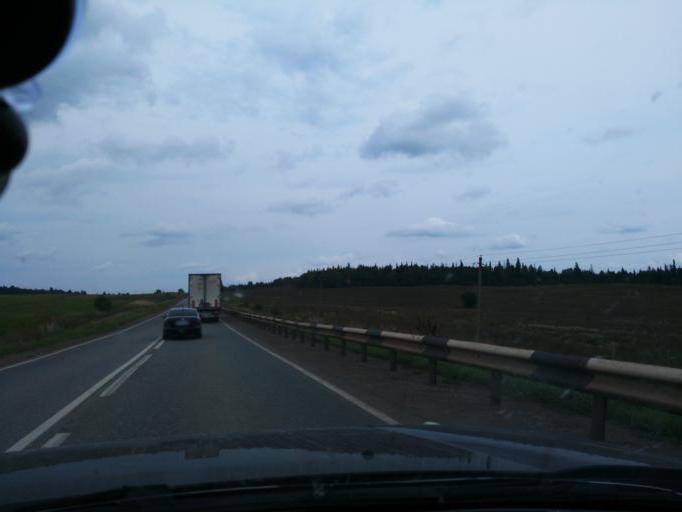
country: RU
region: Perm
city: Kuyeda
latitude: 56.4649
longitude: 55.6670
